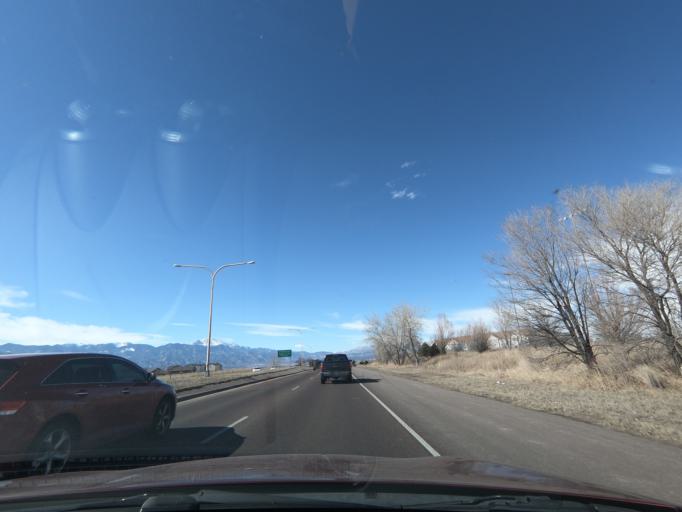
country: US
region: Colorado
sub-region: El Paso County
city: Security-Widefield
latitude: 38.7870
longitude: -104.7256
